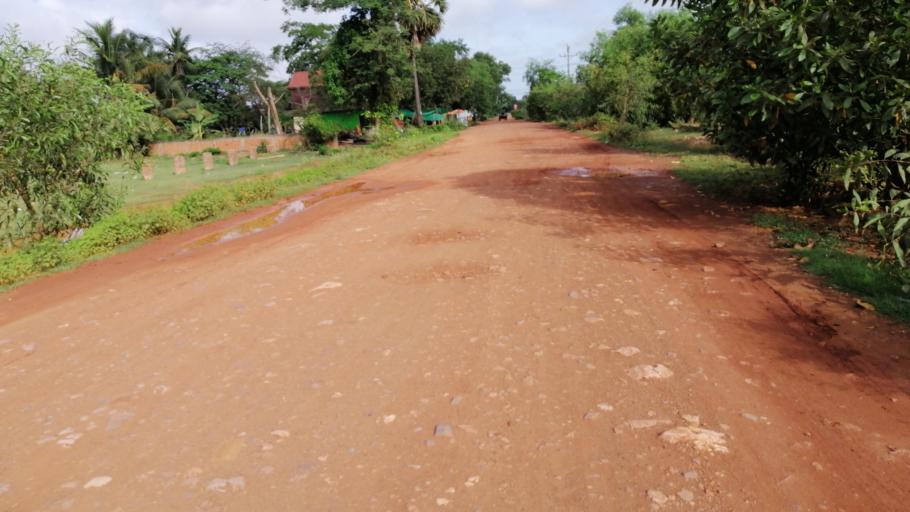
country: KH
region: Siem Reap
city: Siem Reap
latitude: 13.3592
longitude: 103.8271
